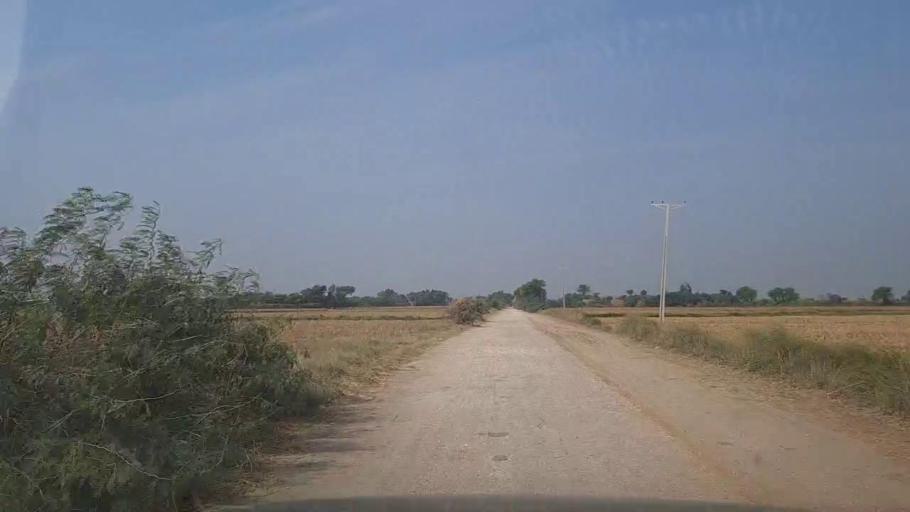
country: PK
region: Sindh
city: Bulri
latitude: 24.9755
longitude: 68.3029
